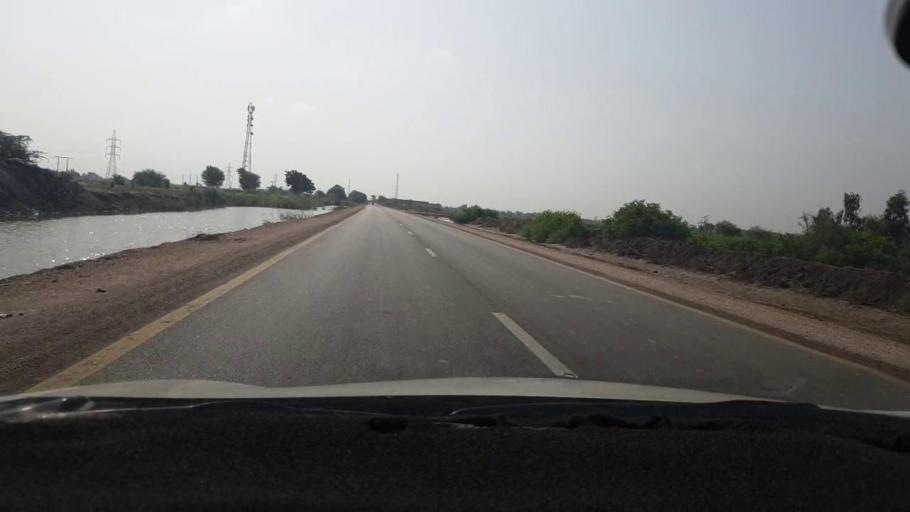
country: PK
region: Sindh
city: Jhol
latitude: 25.8880
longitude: 69.0326
